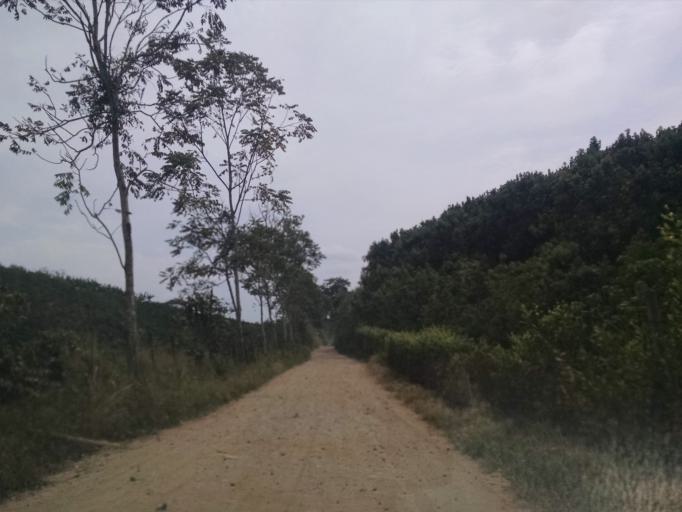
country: CO
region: Valle del Cauca
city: Ulloa
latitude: 4.7078
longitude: -75.7642
